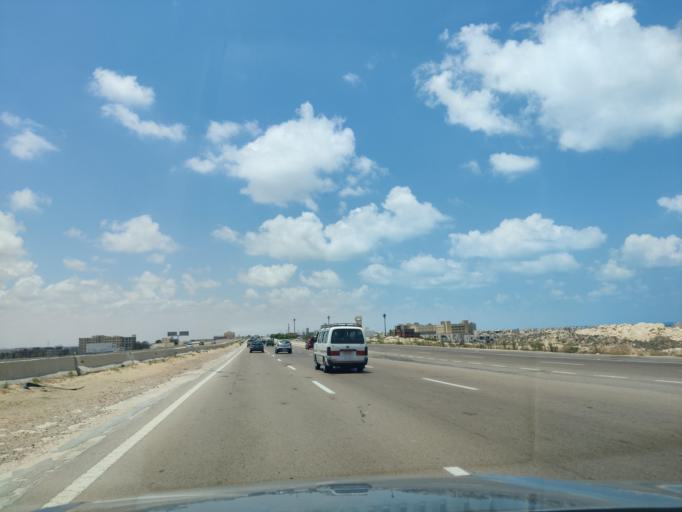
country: EG
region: Muhafazat Matruh
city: Al `Alamayn
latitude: 30.8263
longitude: 29.1976
